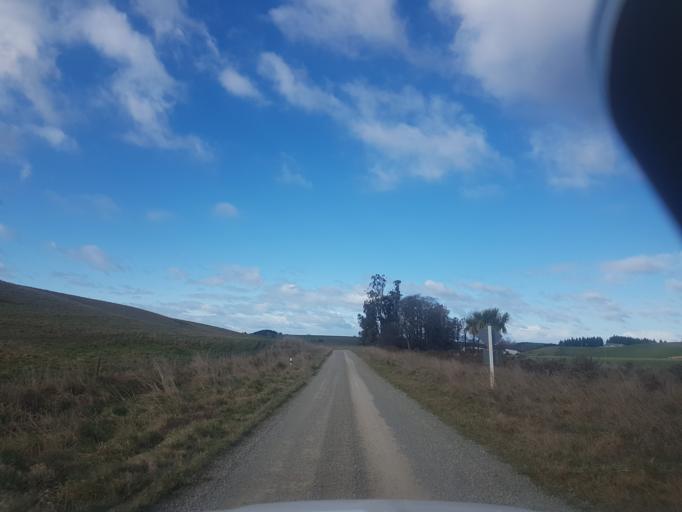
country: NZ
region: Canterbury
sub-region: Timaru District
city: Pleasant Point
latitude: -44.1872
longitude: 171.1901
